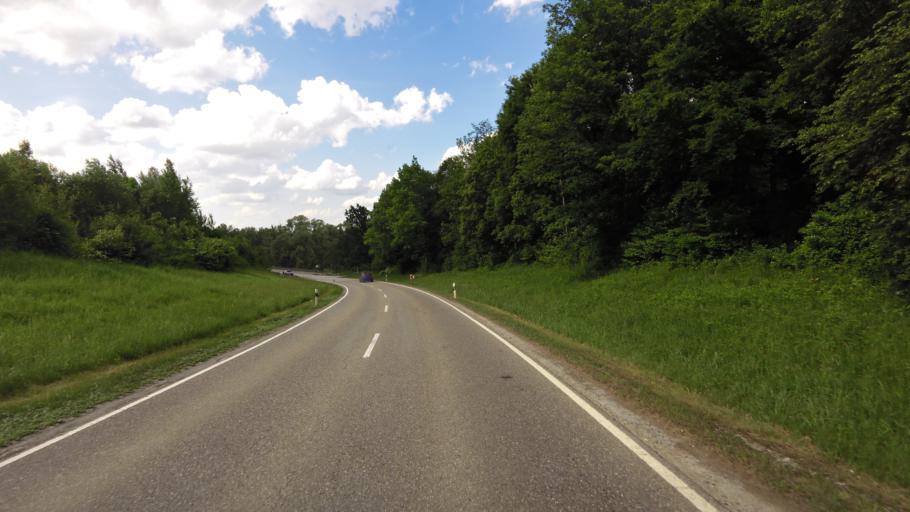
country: DE
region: Bavaria
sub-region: Upper Bavaria
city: Griesstatt
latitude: 47.9923
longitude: 12.1661
